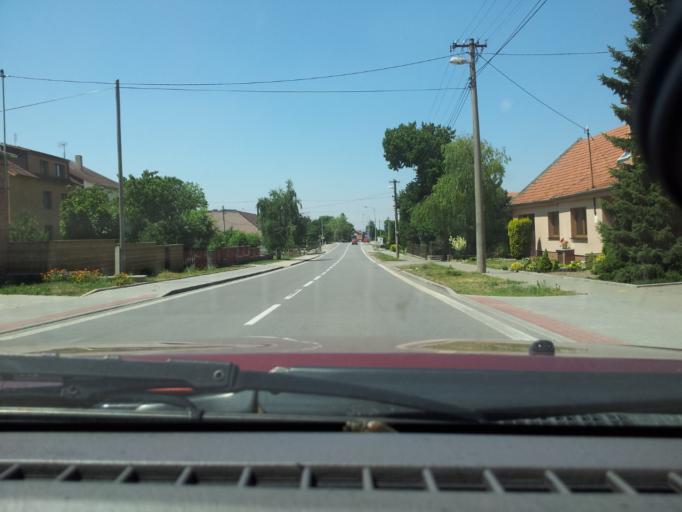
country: CZ
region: South Moravian
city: Tesany
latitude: 49.0383
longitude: 16.7762
